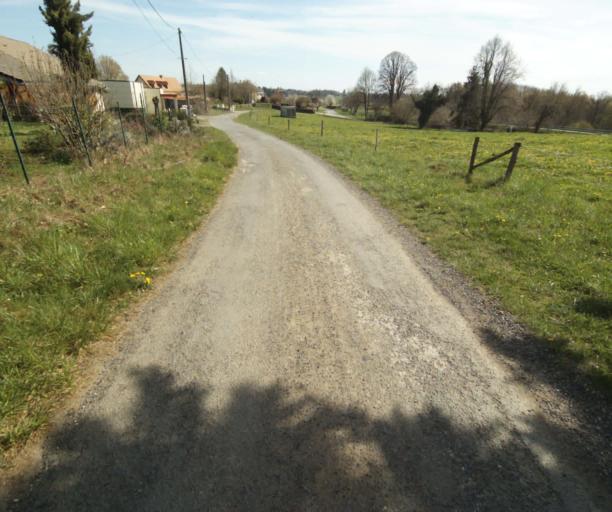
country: FR
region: Limousin
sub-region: Departement de la Correze
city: Seilhac
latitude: 45.3483
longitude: 1.7409
